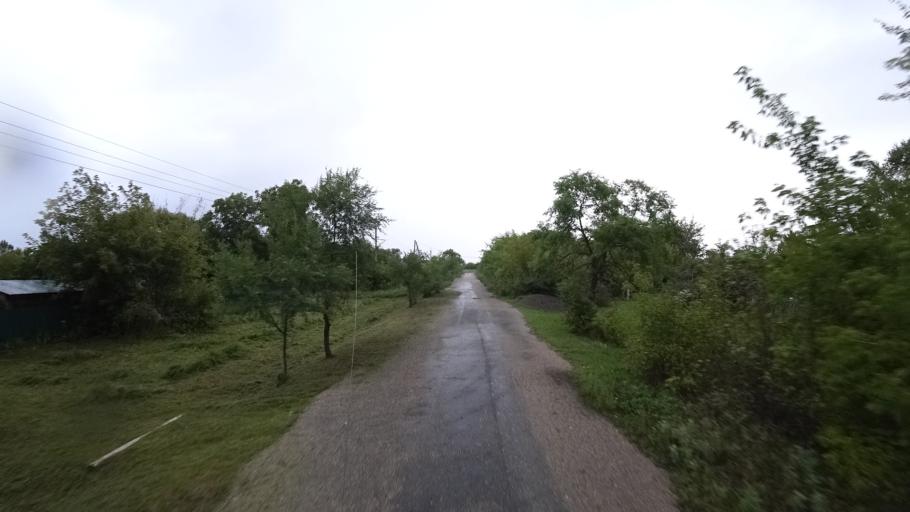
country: RU
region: Primorskiy
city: Chernigovka
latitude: 44.4034
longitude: 132.5316
